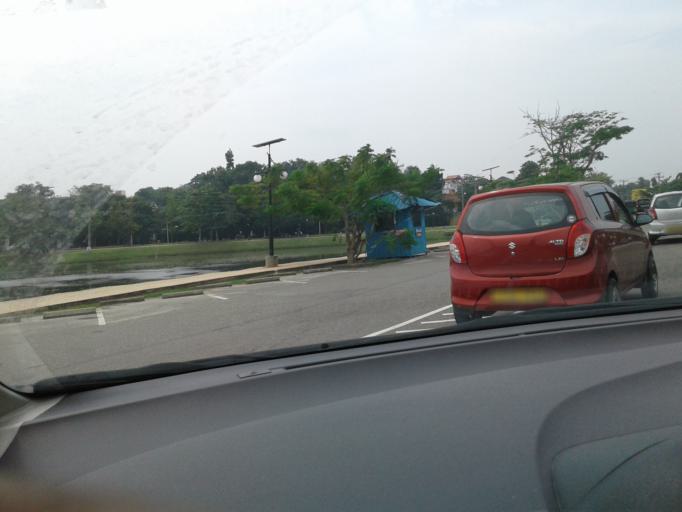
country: LK
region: Western
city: Sri Jayewardenepura Kotte
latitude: 6.8767
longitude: 79.9282
